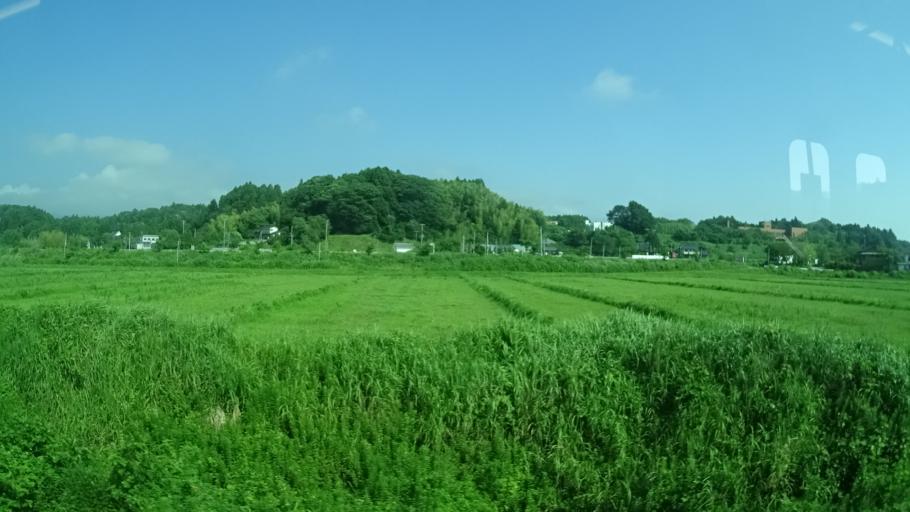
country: JP
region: Fukushima
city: Namie
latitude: 37.3222
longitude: 141.0137
